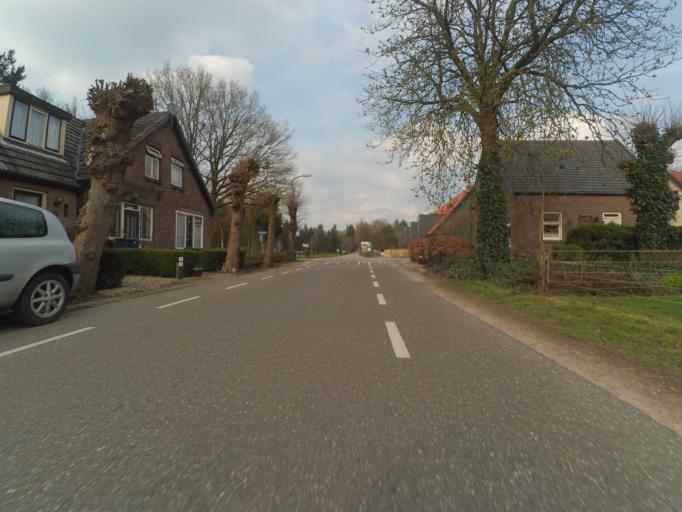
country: NL
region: Gelderland
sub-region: Gemeente Apeldoorn
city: Beekbergen
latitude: 52.1221
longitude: 5.8943
